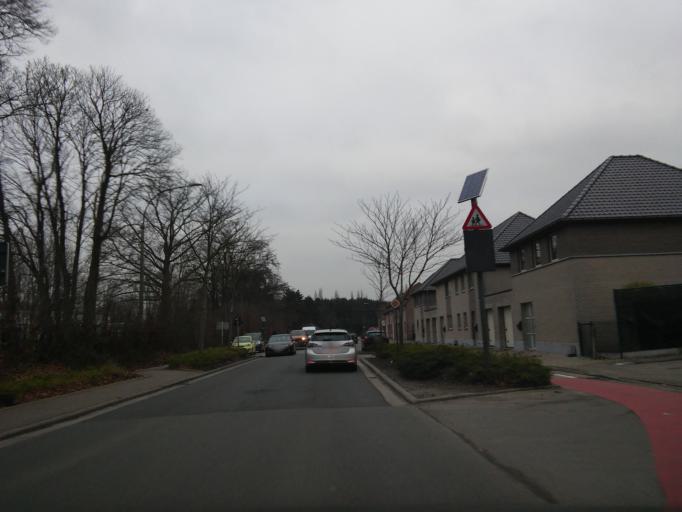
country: BE
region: Flanders
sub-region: Provincie Oost-Vlaanderen
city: Wetteren
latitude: 51.0129
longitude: 3.8810
